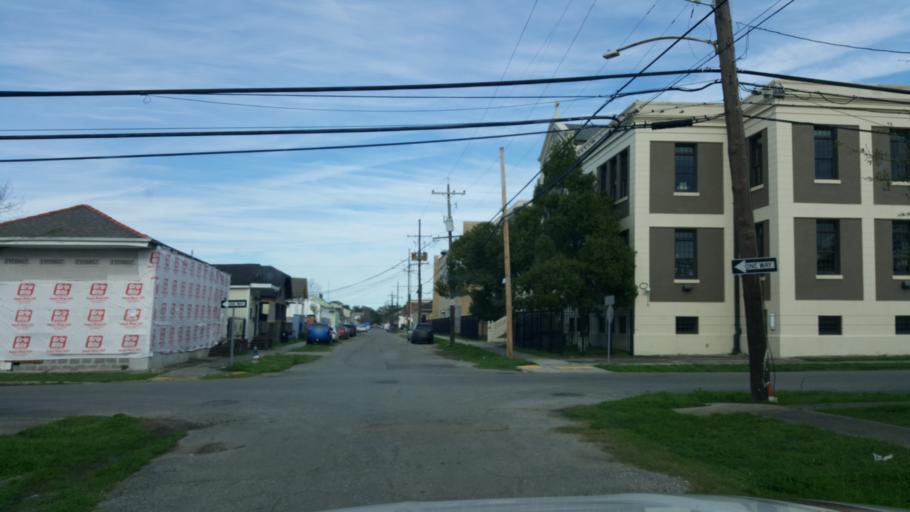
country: US
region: Louisiana
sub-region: Orleans Parish
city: New Orleans
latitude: 29.9758
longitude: -90.0684
